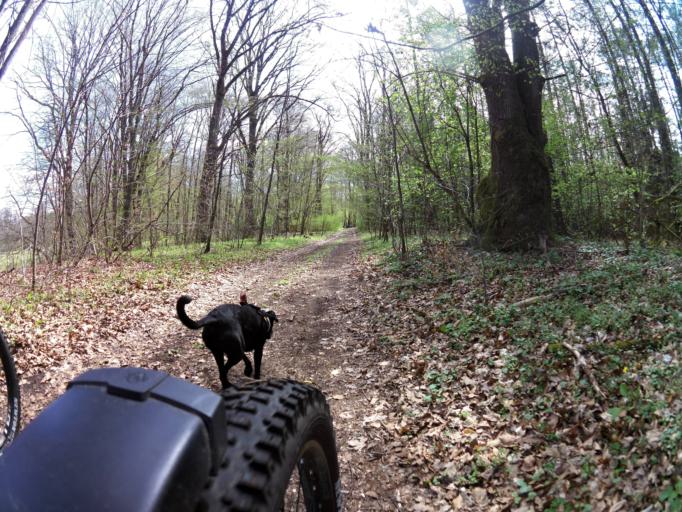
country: PL
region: West Pomeranian Voivodeship
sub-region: Powiat gryficki
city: Ploty
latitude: 53.7508
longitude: 15.3118
